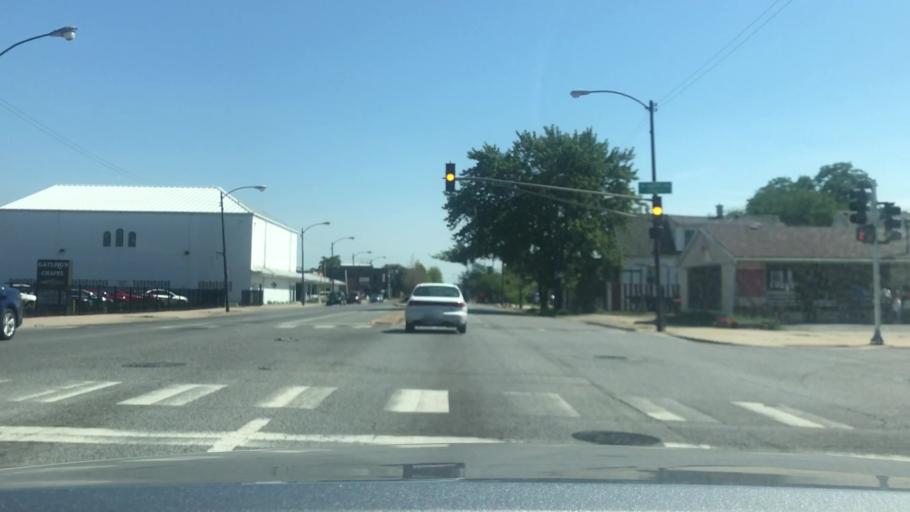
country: US
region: Illinois
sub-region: Cook County
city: Calumet Park
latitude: 41.7107
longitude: -87.6430
